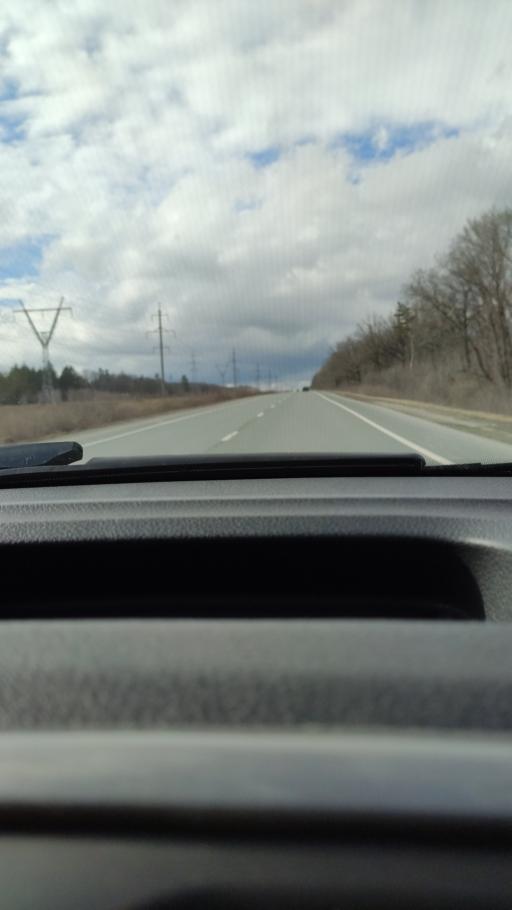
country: RU
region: Samara
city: Bogatyr'
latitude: 53.4980
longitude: 49.9578
